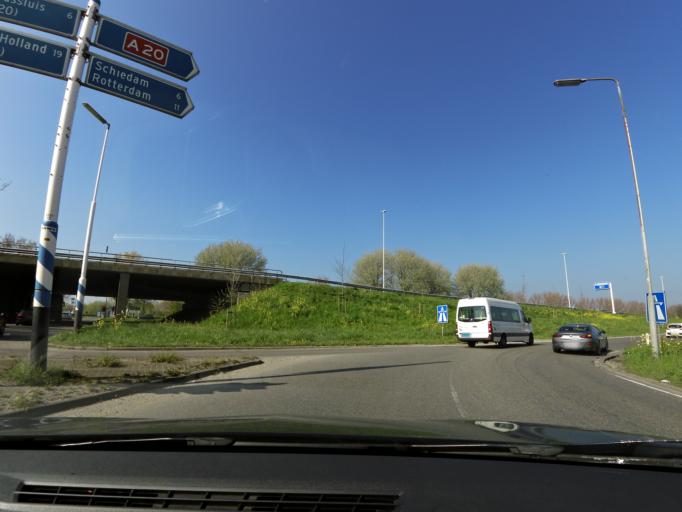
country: NL
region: South Holland
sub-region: Gemeente Vlaardingen
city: Vlaardingen
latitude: 51.9176
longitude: 4.3313
